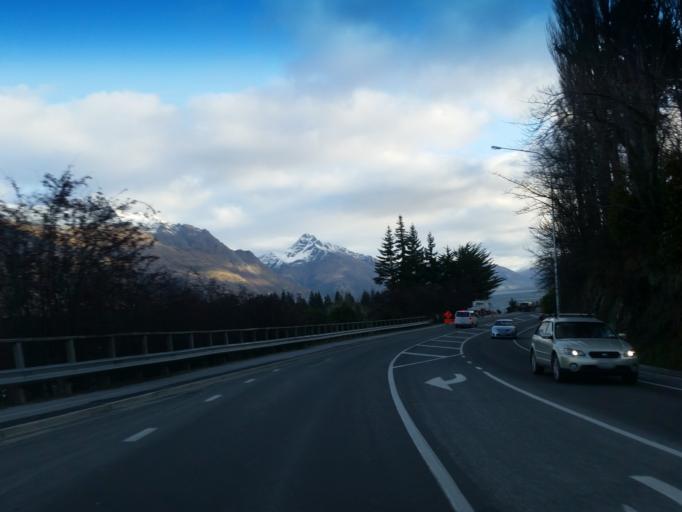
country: NZ
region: Otago
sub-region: Queenstown-Lakes District
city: Queenstown
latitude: -45.0332
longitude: 168.6819
